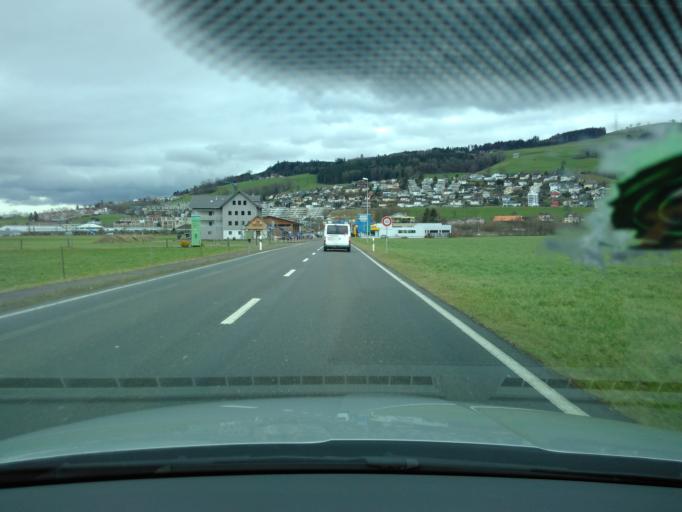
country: CH
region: Lucerne
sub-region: Lucerne-Land District
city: Root
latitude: 47.1249
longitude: 8.3874
